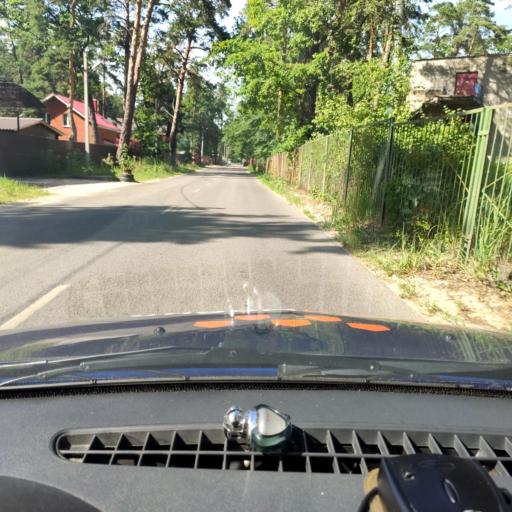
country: RU
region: Voronezj
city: Somovo
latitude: 51.7536
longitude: 39.3661
